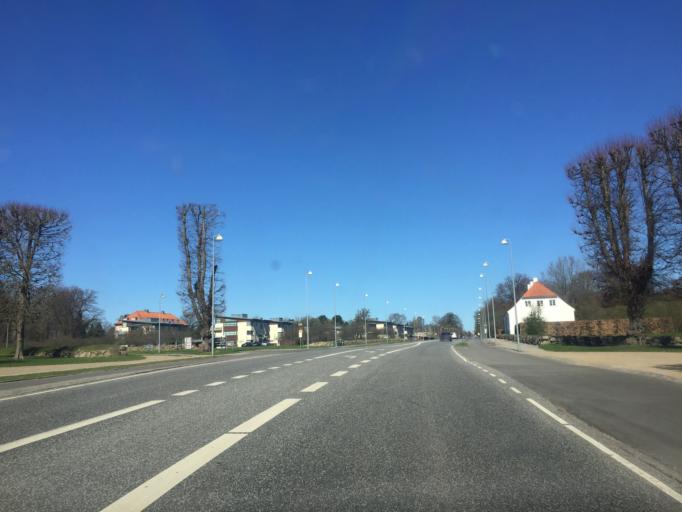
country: DK
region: Capital Region
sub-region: Lyngby-Tarbaek Kommune
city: Kongens Lyngby
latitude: 55.7784
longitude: 12.4944
